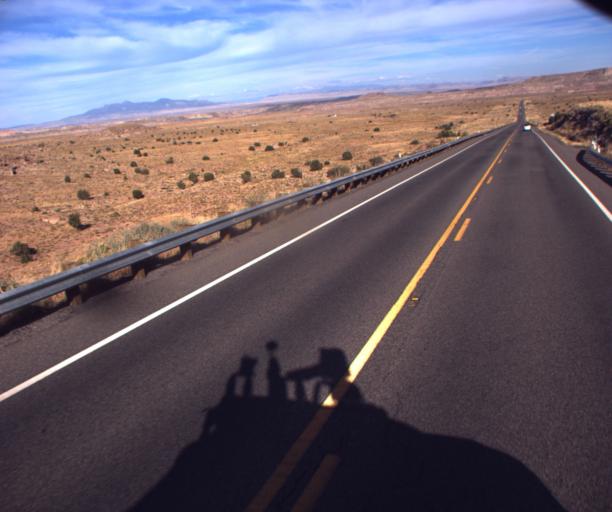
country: US
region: New Mexico
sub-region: San Juan County
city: Shiprock
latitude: 36.9290
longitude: -109.1595
